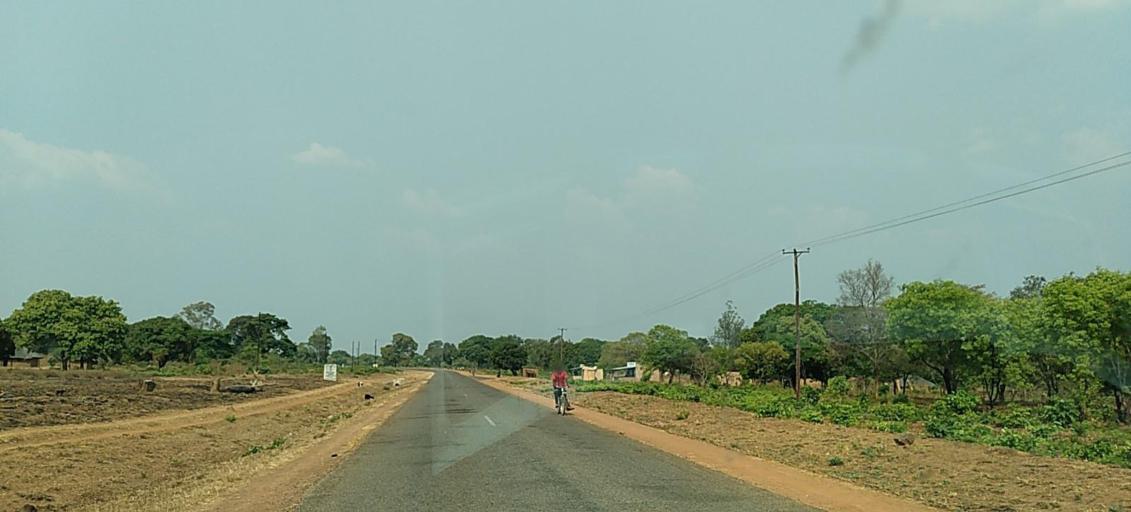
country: ZM
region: North-Western
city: Kabompo
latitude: -13.5352
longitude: 24.2799
